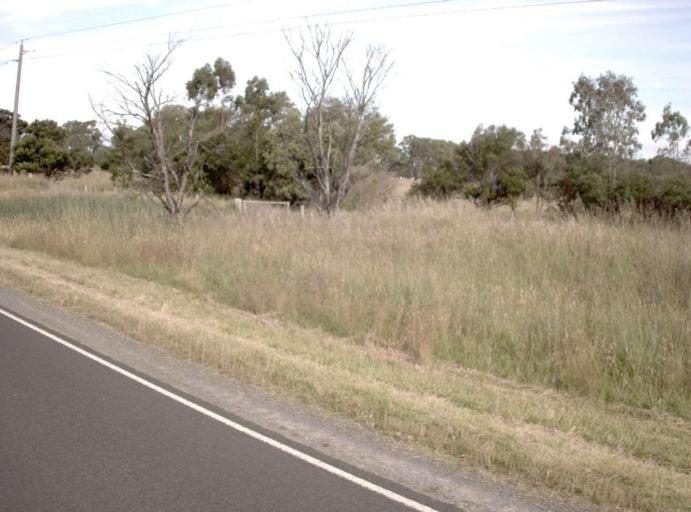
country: AU
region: Victoria
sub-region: Wellington
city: Heyfield
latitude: -38.0592
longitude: 146.6590
